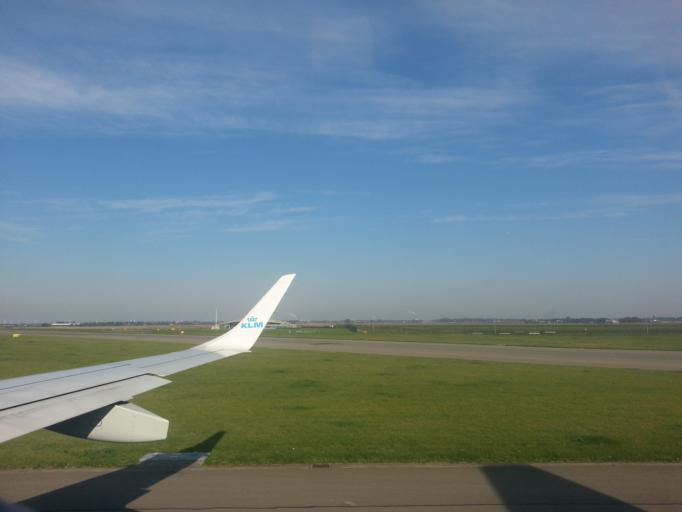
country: NL
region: North Holland
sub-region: Gemeente Haarlemmermeer
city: Hoofddorp
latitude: 52.3331
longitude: 4.7110
